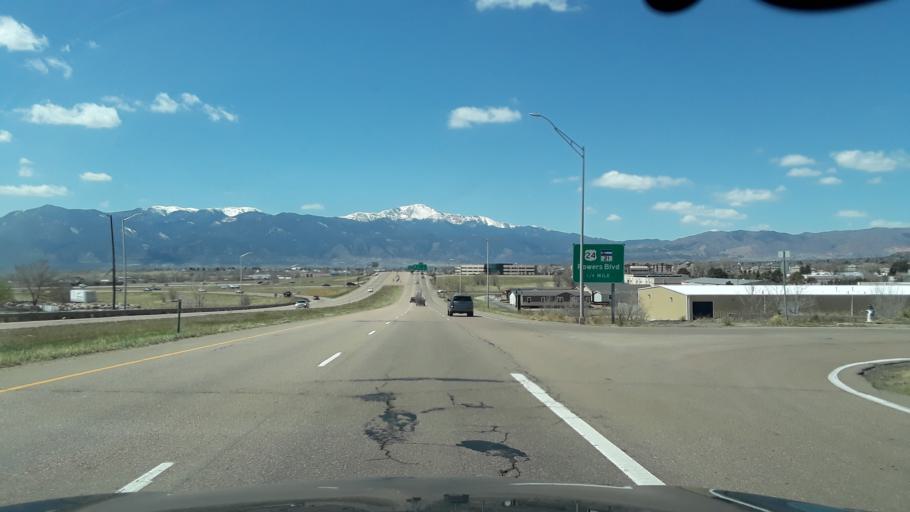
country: US
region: Colorado
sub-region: El Paso County
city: Cimarron Hills
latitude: 38.8391
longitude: -104.7138
